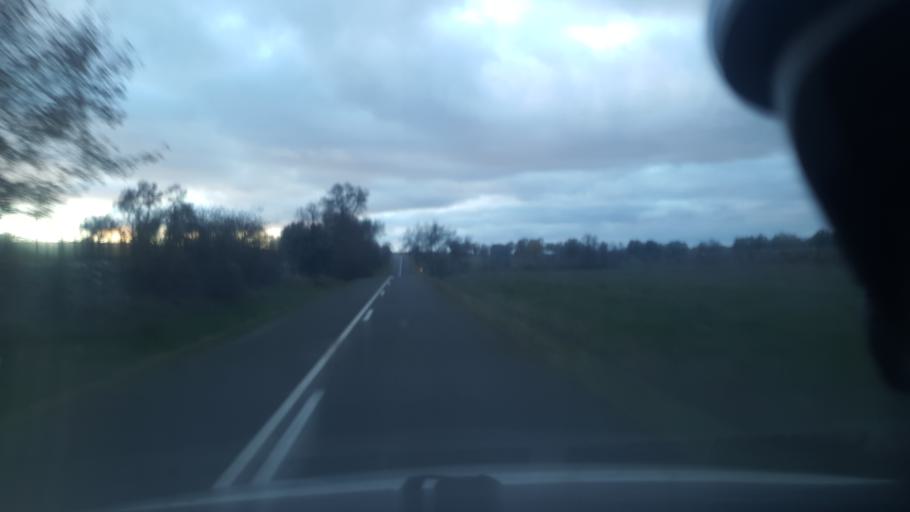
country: ES
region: Castille and Leon
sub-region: Provincia de Segovia
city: Vegas de Matute
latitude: 40.7092
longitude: -4.3210
